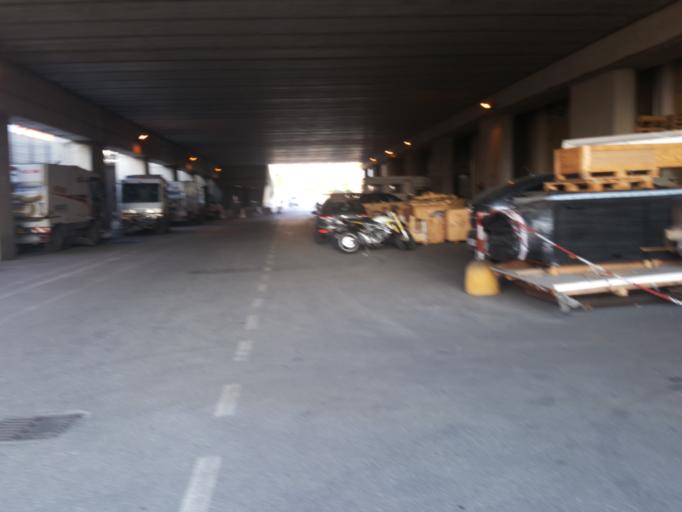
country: IT
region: Liguria
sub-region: Provincia di Genova
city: San Teodoro
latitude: 44.4066
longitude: 8.9098
